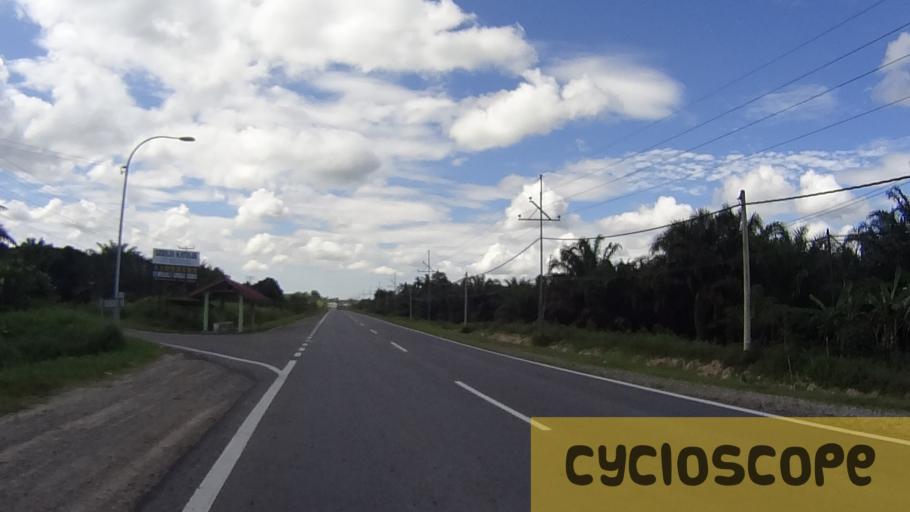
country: MY
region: Sabah
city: Beaufort
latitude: 5.2981
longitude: 115.6945
